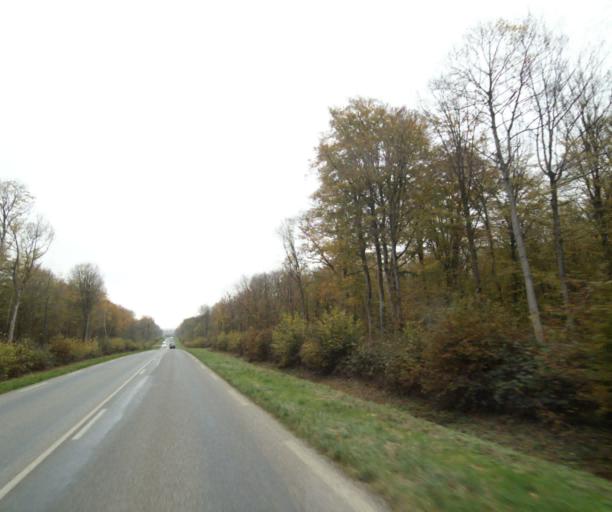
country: FR
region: Lorraine
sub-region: Departement de Meurthe-et-Moselle
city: Moutiers
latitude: 49.2393
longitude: 5.9706
